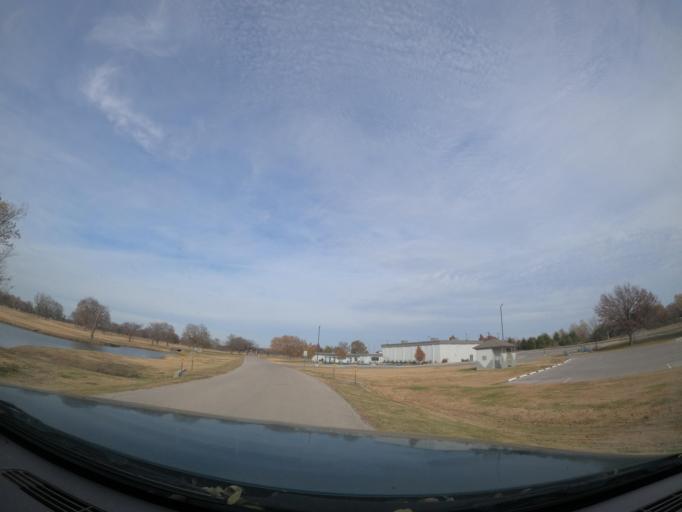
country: US
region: Oklahoma
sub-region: Tulsa County
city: Turley
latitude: 36.2445
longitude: -95.9555
